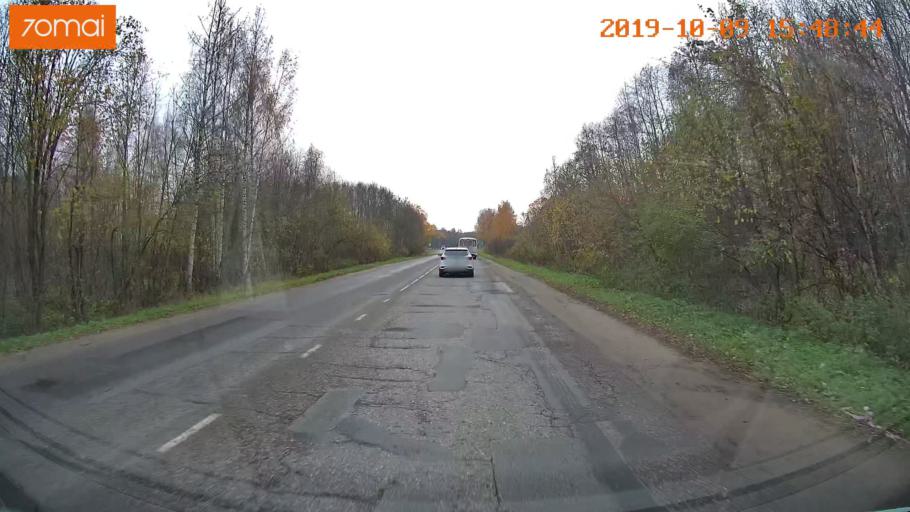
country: RU
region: Kostroma
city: Oktyabr'skiy
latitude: 57.8098
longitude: 41.0119
